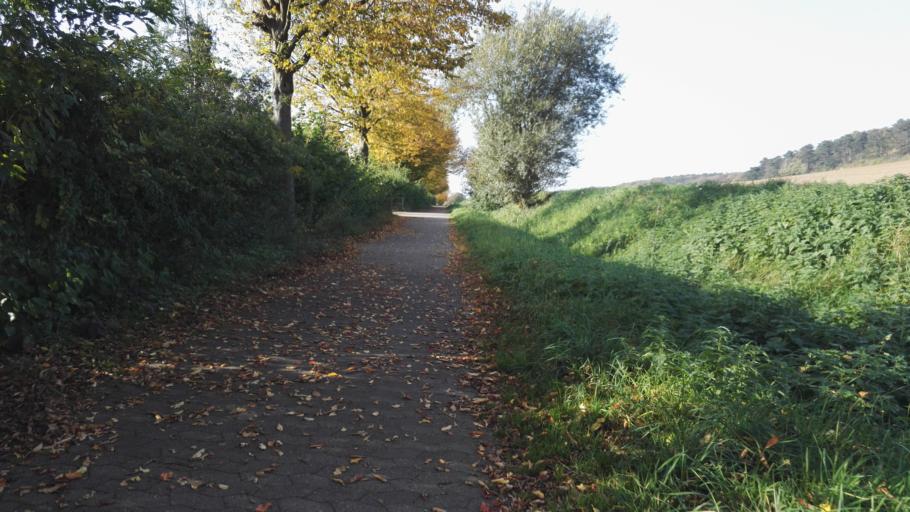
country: DE
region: Lower Saxony
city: Hildesheim
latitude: 52.1322
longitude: 9.9894
